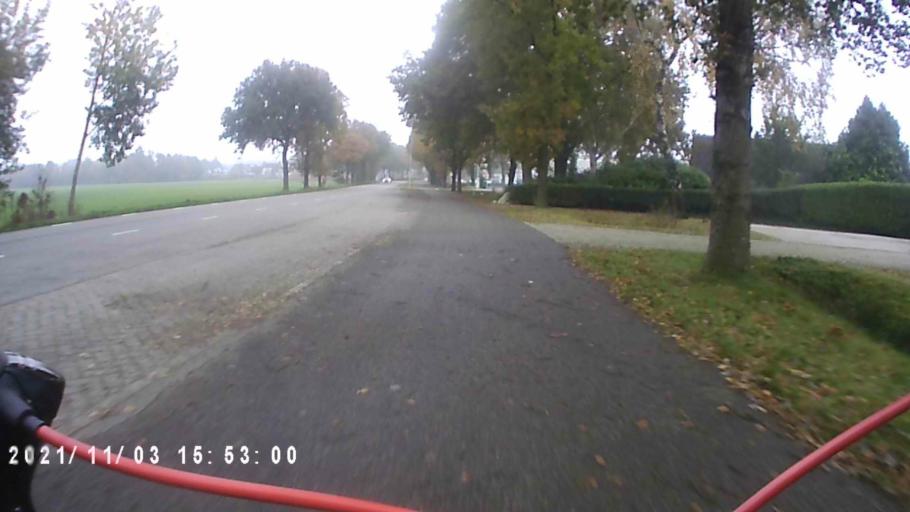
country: NL
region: Groningen
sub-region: Gemeente Leek
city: Leek
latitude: 53.0729
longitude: 6.3316
